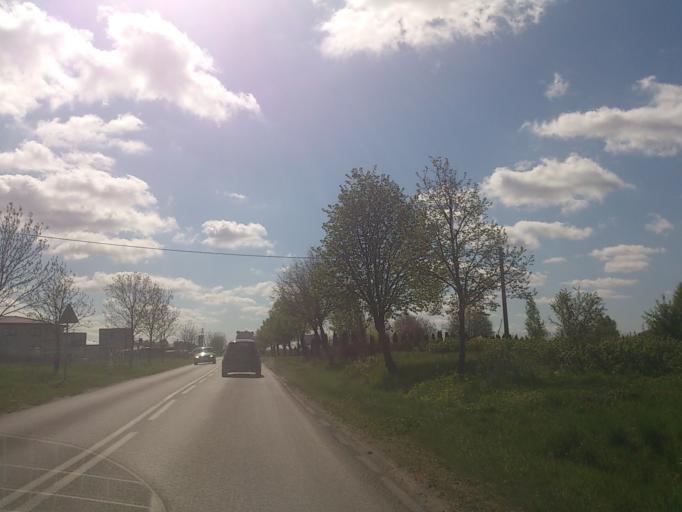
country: PL
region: Warmian-Masurian Voivodeship
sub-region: Powiat dzialdowski
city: Dzialdowo
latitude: 53.2256
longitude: 20.2002
